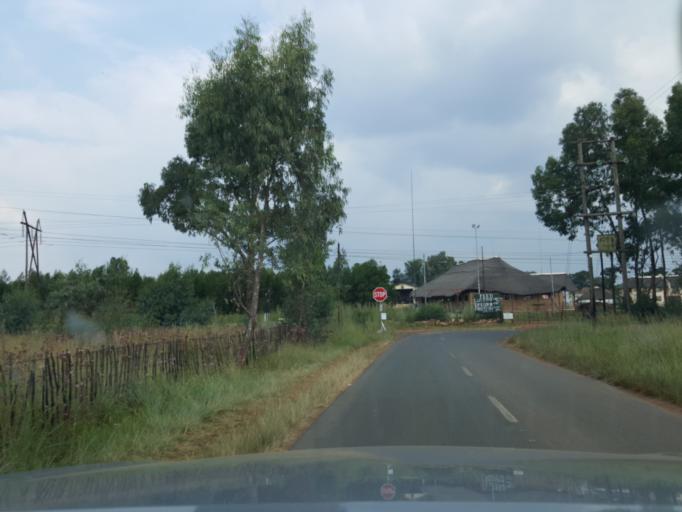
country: ZA
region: Gauteng
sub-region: City of Tshwane Metropolitan Municipality
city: Centurion
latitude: -25.8707
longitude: 28.3333
